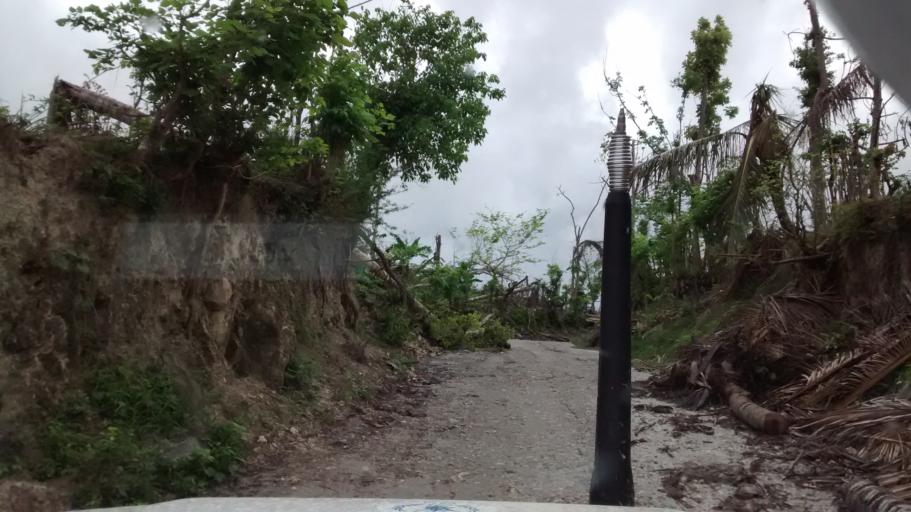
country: HT
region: Grandans
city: Jeremie
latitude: 18.5860
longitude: -74.1453
